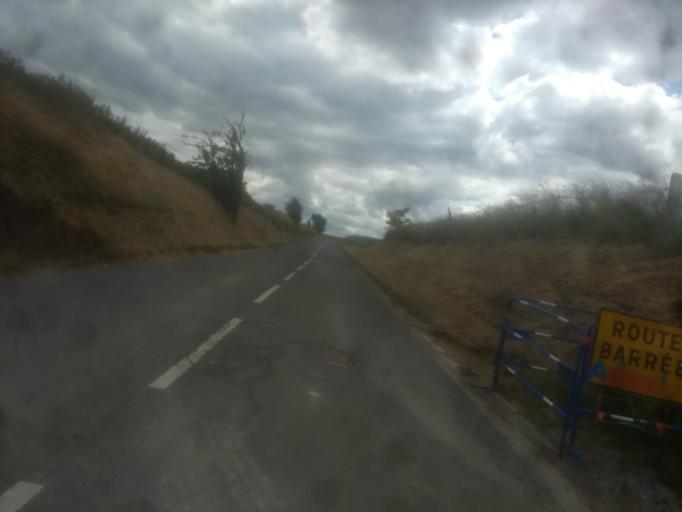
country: FR
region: Nord-Pas-de-Calais
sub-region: Departement du Pas-de-Calais
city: Agny
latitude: 50.2431
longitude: 2.7272
